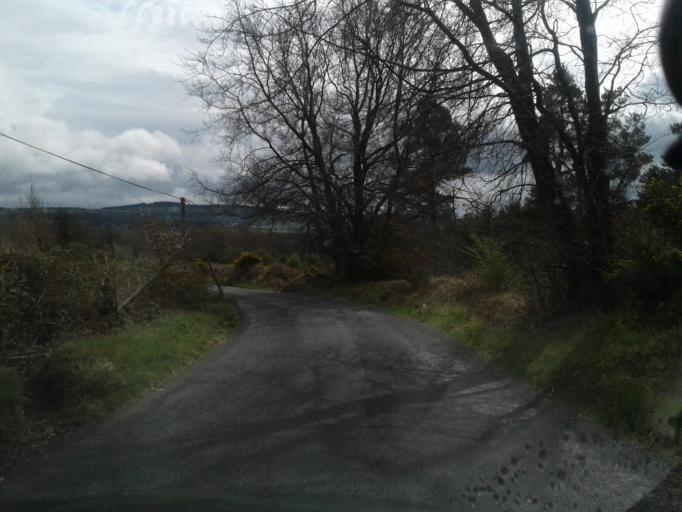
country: IE
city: Newtownmountkennedy
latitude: 53.0915
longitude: -6.2274
